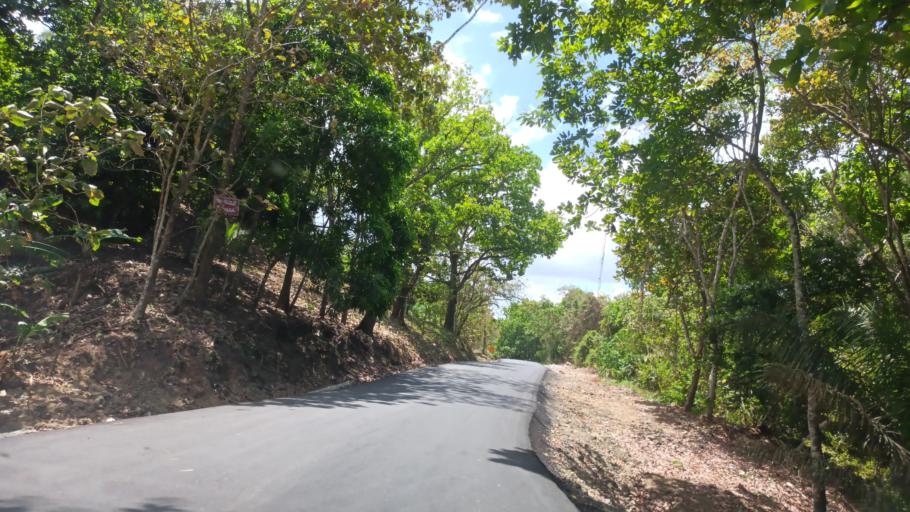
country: PA
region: Panama
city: Alcalde Diaz
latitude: 9.0960
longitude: -79.5755
